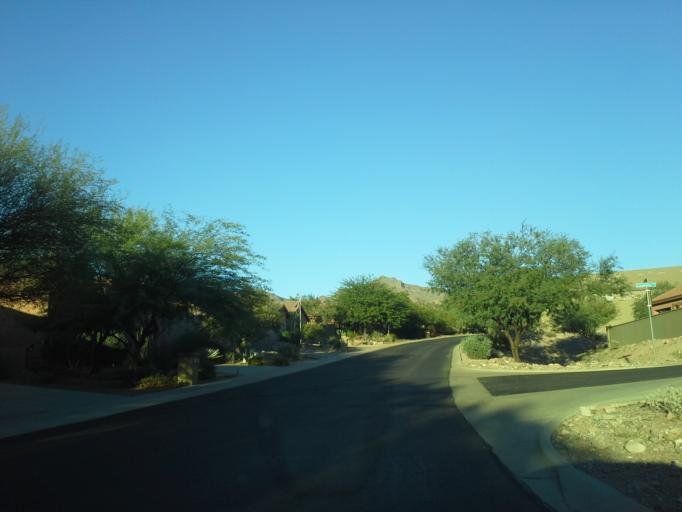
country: US
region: Arizona
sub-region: Pinal County
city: Apache Junction
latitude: 33.3762
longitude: -111.4592
